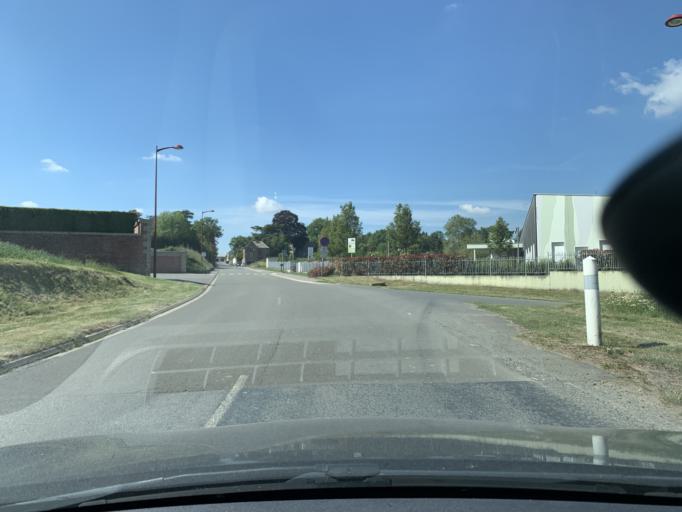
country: FR
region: Nord-Pas-de-Calais
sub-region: Departement du Pas-de-Calais
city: Oisy-le-Verger
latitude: 50.2551
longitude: 3.1267
